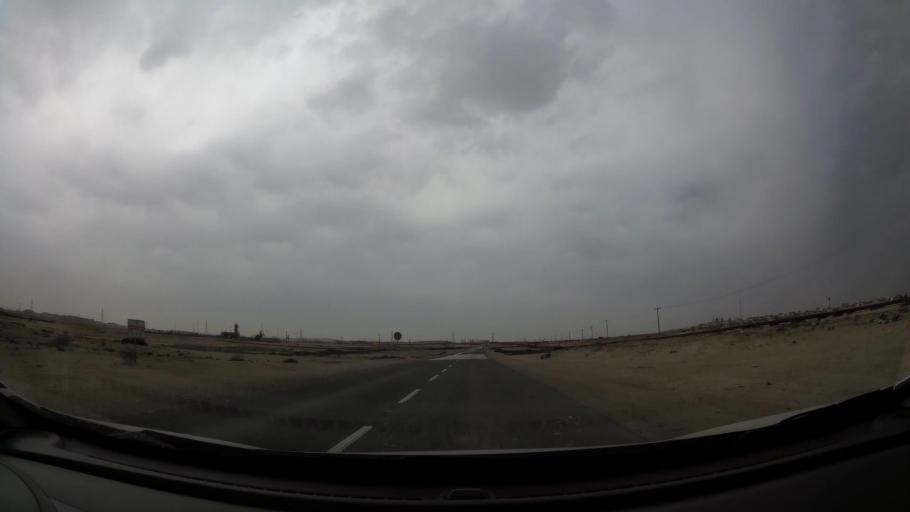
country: BH
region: Northern
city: Ar Rifa'
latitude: 26.0838
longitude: 50.5654
